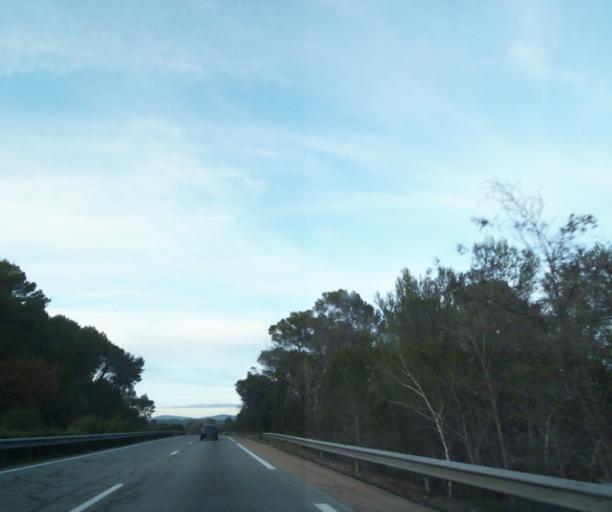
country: FR
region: Provence-Alpes-Cote d'Azur
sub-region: Departement du Var
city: La Motte
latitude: 43.4859
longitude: 6.5089
